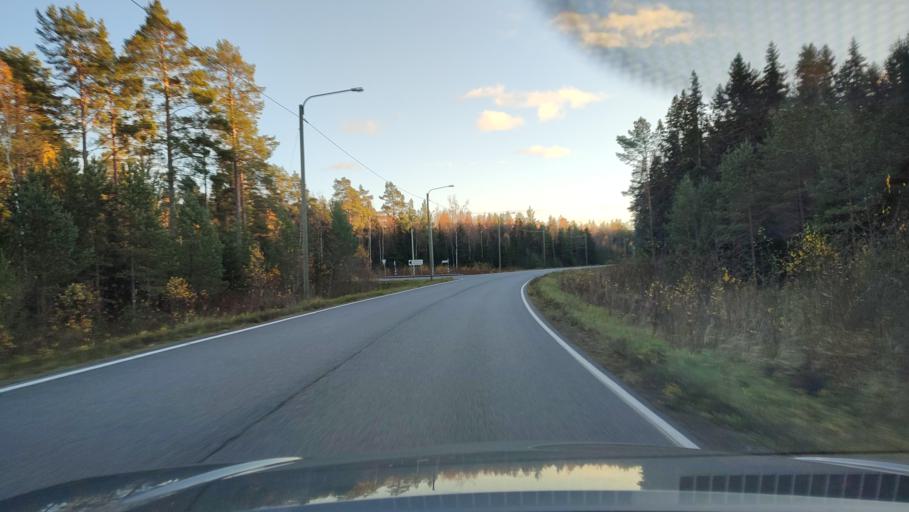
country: FI
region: Ostrobothnia
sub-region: Sydosterbotten
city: Kristinestad
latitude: 62.2635
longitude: 21.3488
